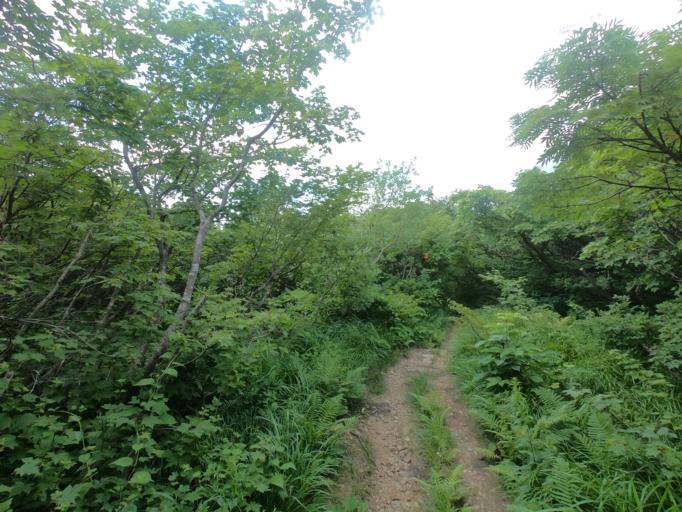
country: JP
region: Akita
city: Yuzawa
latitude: 38.9771
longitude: 140.7732
